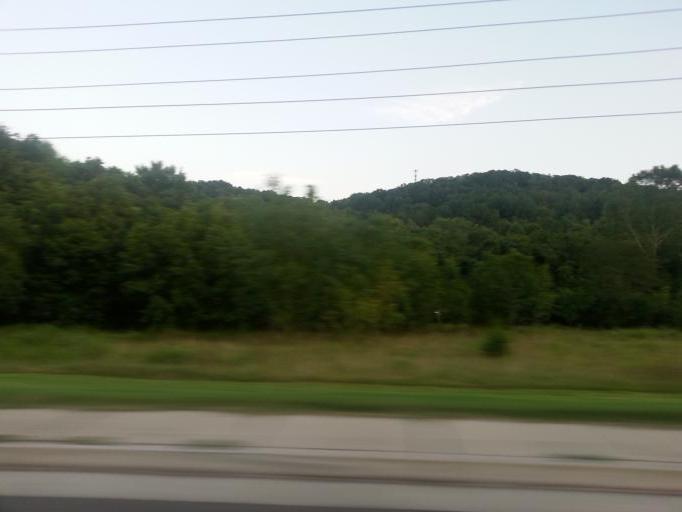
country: US
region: Tennessee
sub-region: Anderson County
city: Oak Ridge
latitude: 36.0058
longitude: -84.2814
